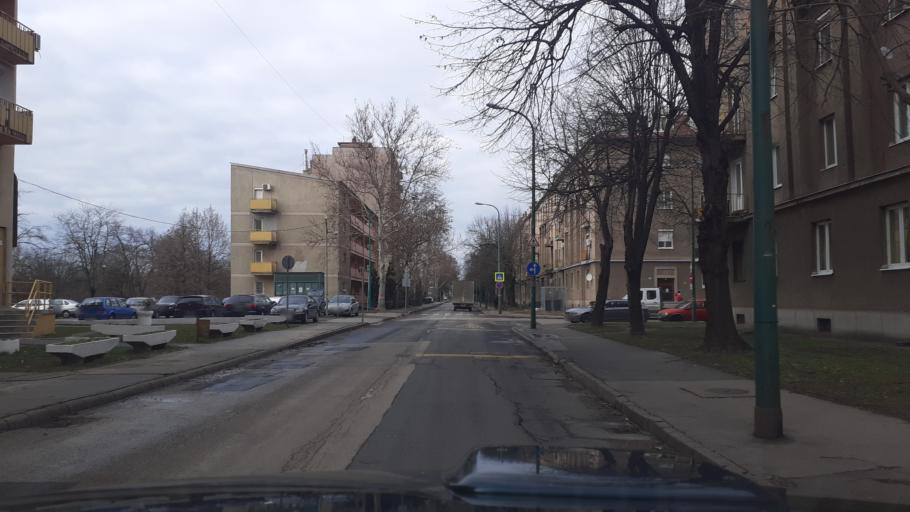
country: HU
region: Fejer
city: dunaujvaros
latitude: 46.9632
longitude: 18.9286
